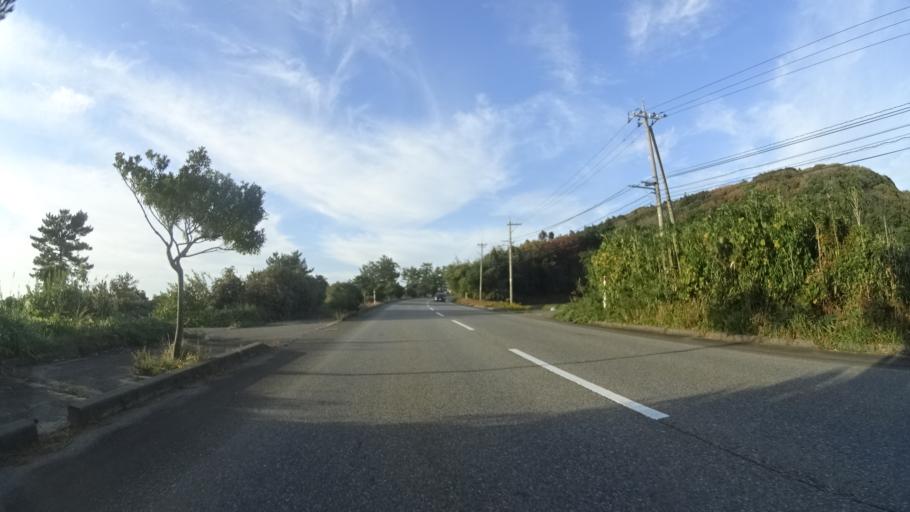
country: JP
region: Ishikawa
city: Hakui
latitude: 37.1055
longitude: 136.7294
